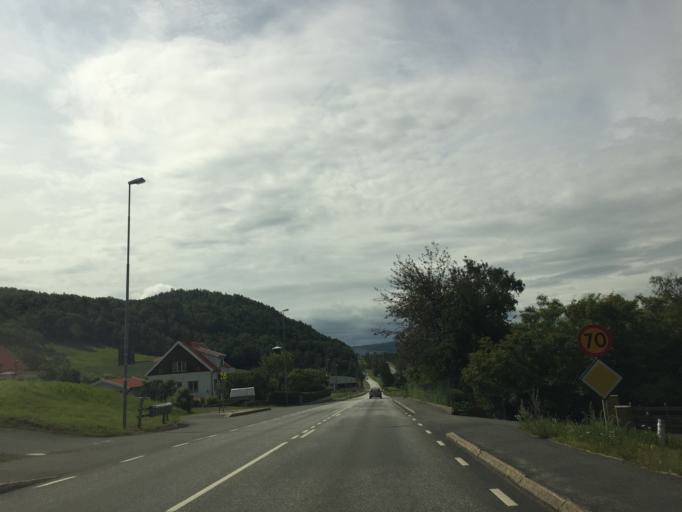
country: SE
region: Joenkoeping
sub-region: Jonkopings Kommun
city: Kaxholmen
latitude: 57.8370
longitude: 14.2728
